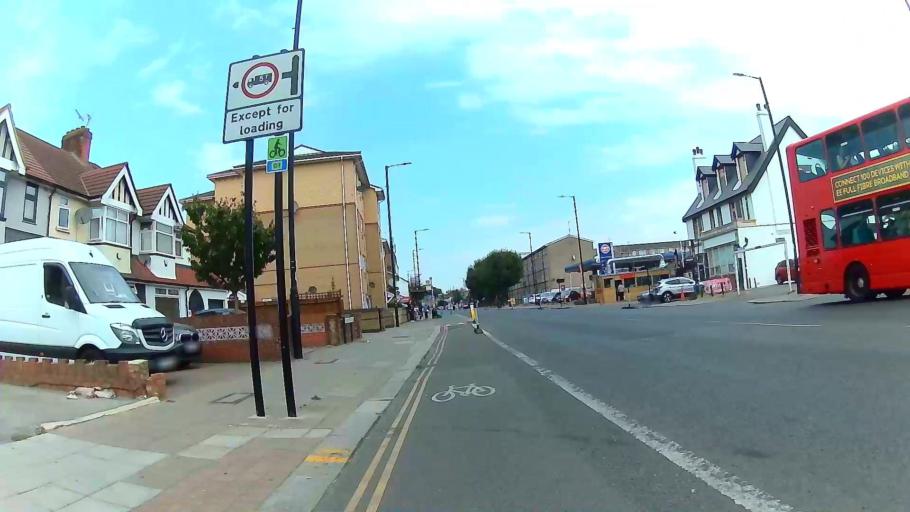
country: GB
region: England
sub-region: Greater London
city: Enfield
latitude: 51.6401
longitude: -0.0478
